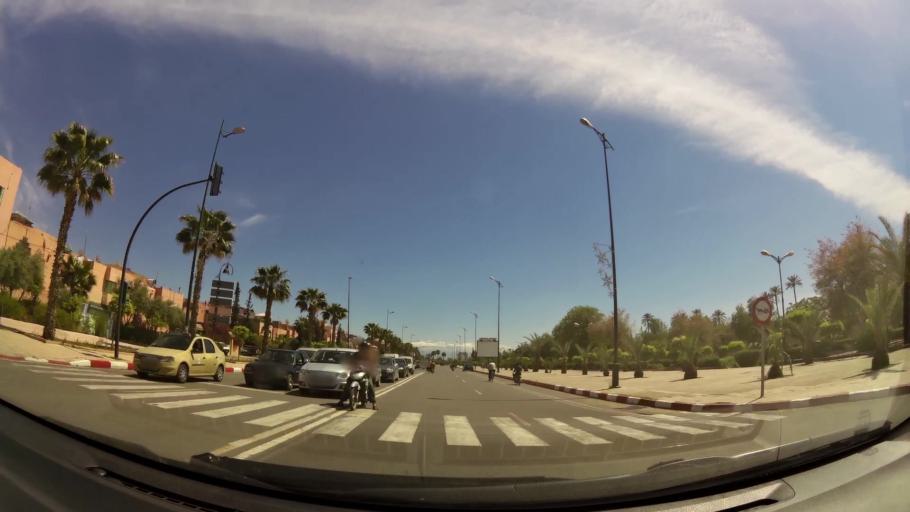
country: MA
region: Marrakech-Tensift-Al Haouz
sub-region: Marrakech
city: Marrakesh
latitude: 31.6037
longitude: -7.9718
